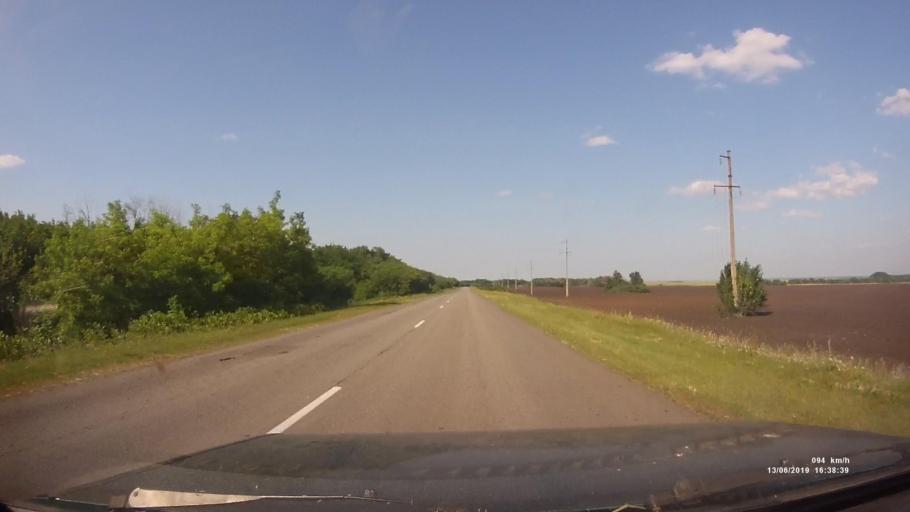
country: RU
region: Rostov
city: Kazanskaya
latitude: 49.9210
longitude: 41.3268
